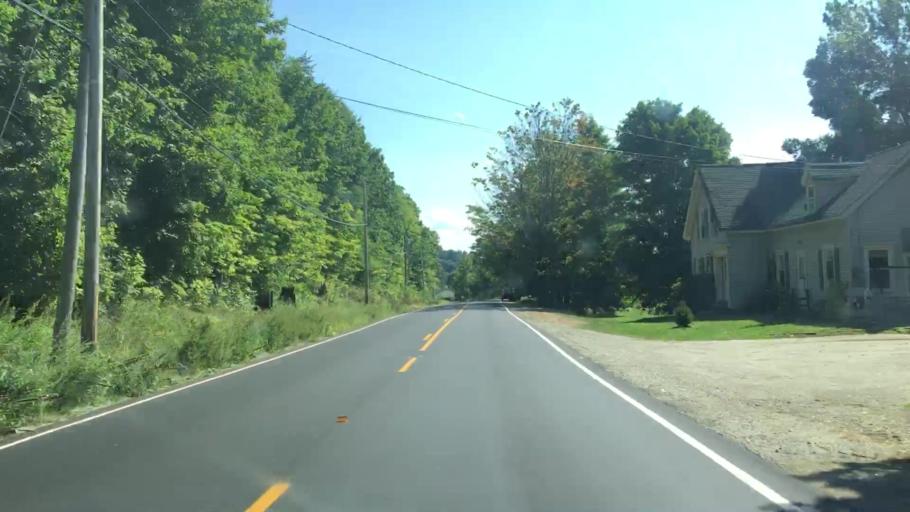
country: US
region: Maine
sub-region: Androscoggin County
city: Sabattus
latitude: 44.1333
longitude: -70.0876
